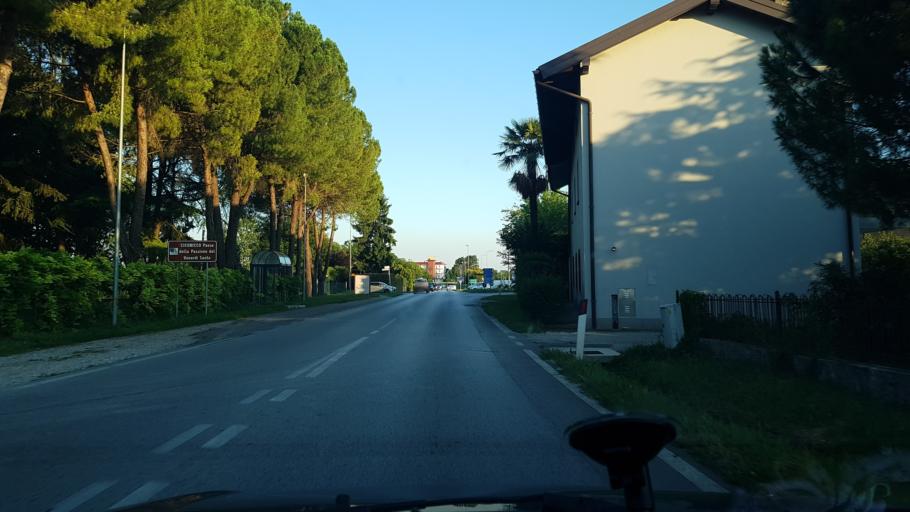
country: IT
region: Friuli Venezia Giulia
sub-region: Provincia di Udine
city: Fagagna
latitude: 46.1021
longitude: 13.0952
